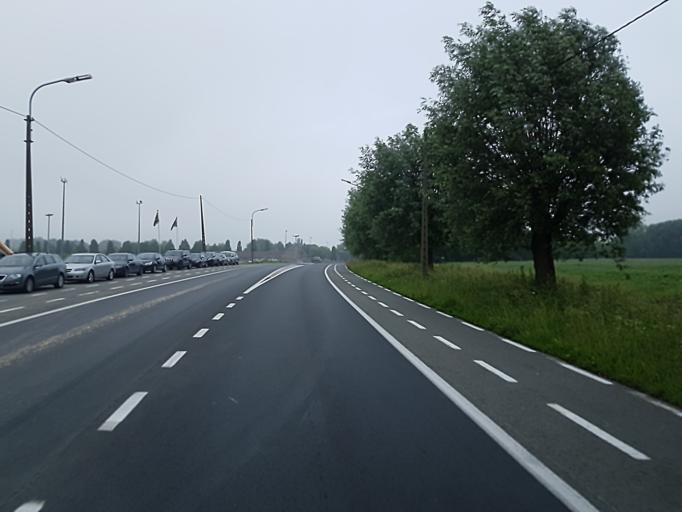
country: BE
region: Flanders
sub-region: Provincie West-Vlaanderen
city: Kortrijk
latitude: 50.7969
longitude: 3.2418
